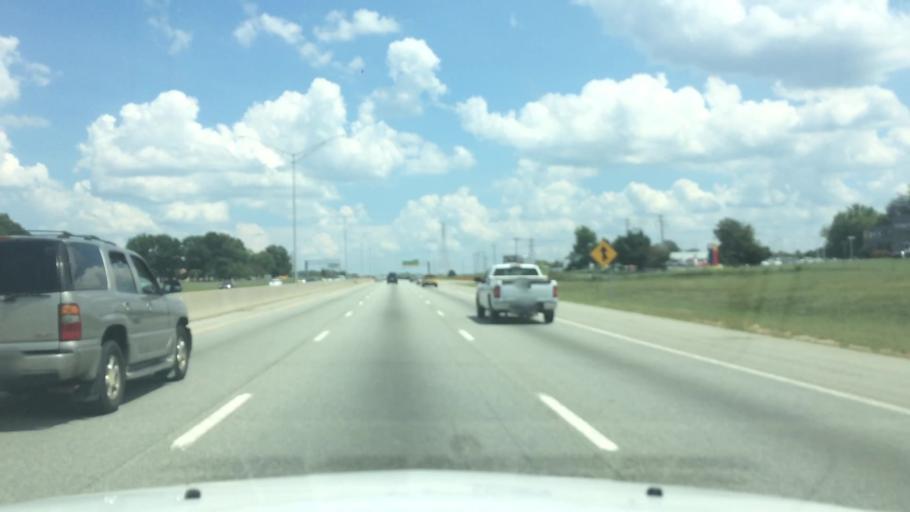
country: US
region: North Carolina
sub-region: Guilford County
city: Jamestown
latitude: 36.0648
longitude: -79.9144
